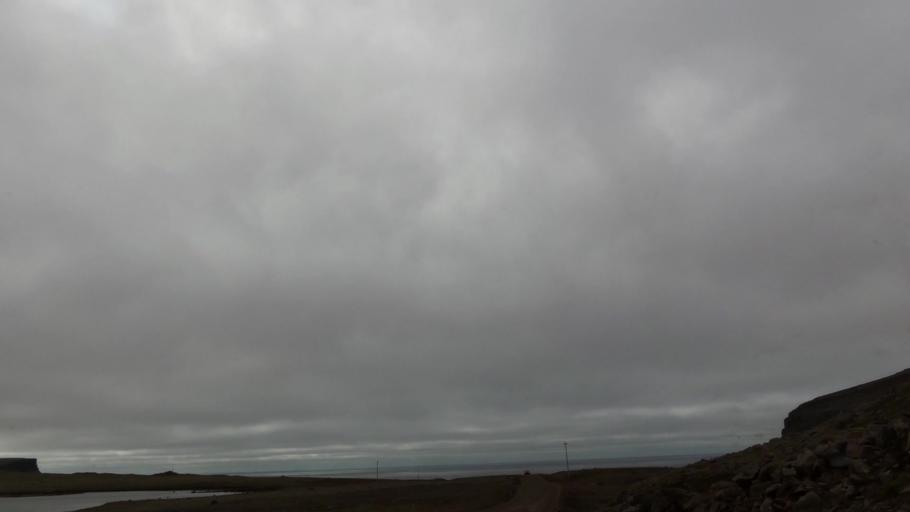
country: IS
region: West
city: Olafsvik
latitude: 65.5275
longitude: -24.4356
